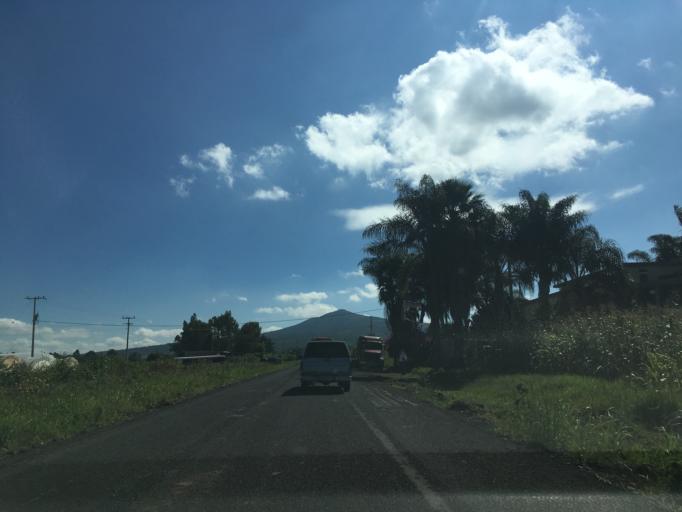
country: MX
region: Mexico
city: Tlazazalca
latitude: 19.9724
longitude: -102.0690
